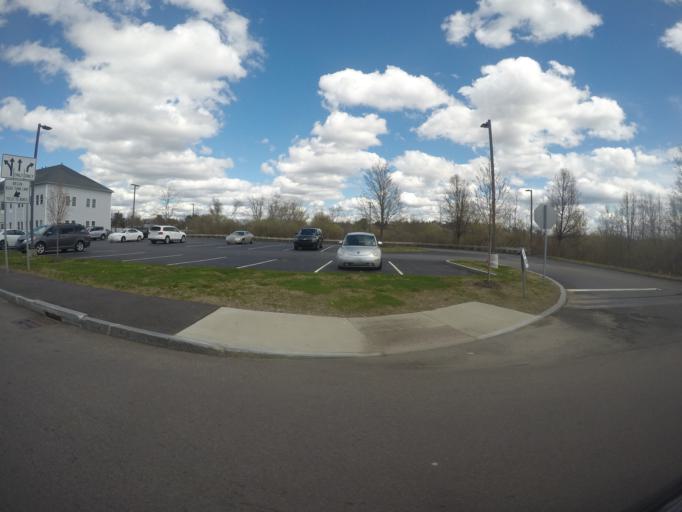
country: US
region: Massachusetts
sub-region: Plymouth County
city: West Bridgewater
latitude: 42.0099
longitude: -71.0668
